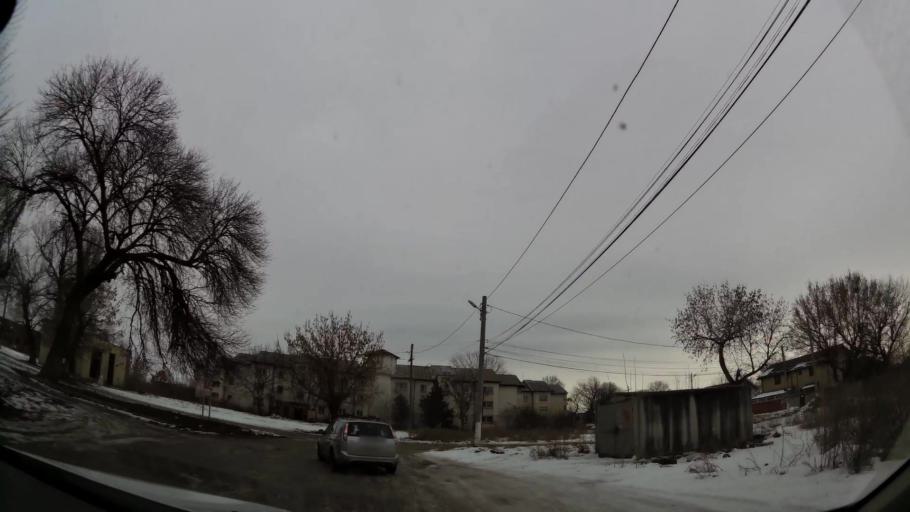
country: RO
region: Ilfov
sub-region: Comuna Pantelimon
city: Pantelimon
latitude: 44.4665
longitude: 26.2084
